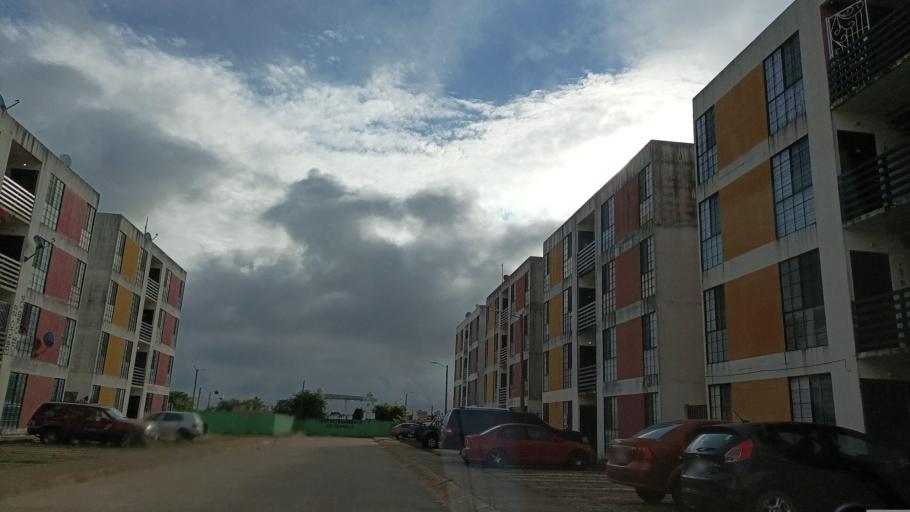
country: MX
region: Veracruz
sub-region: Coatzacoalcos
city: Fraccionamiento Ciudad Olmeca
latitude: 18.1561
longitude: -94.5588
